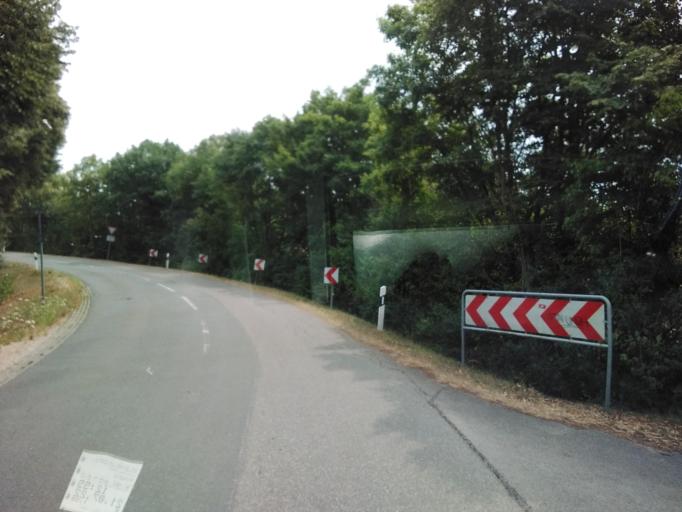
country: DE
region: Bavaria
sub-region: Regierungsbezirk Mittelfranken
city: Hilpoltstein
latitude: 49.2257
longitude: 11.1976
